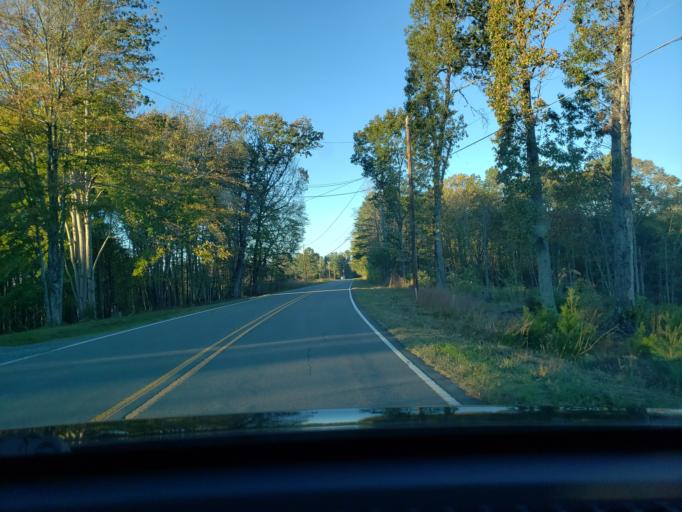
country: US
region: North Carolina
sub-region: Forsyth County
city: Walkertown
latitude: 36.2326
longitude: -80.2008
